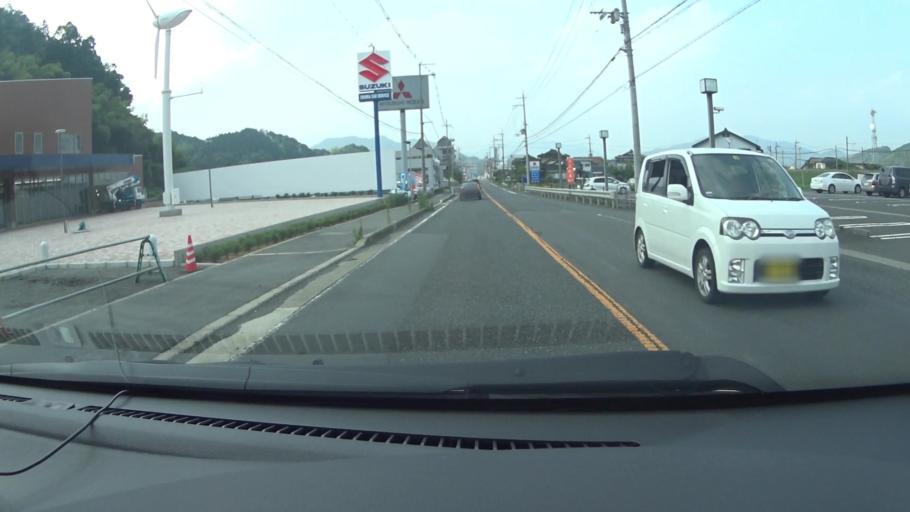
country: JP
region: Kyoto
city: Maizuru
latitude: 35.4211
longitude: 135.3300
